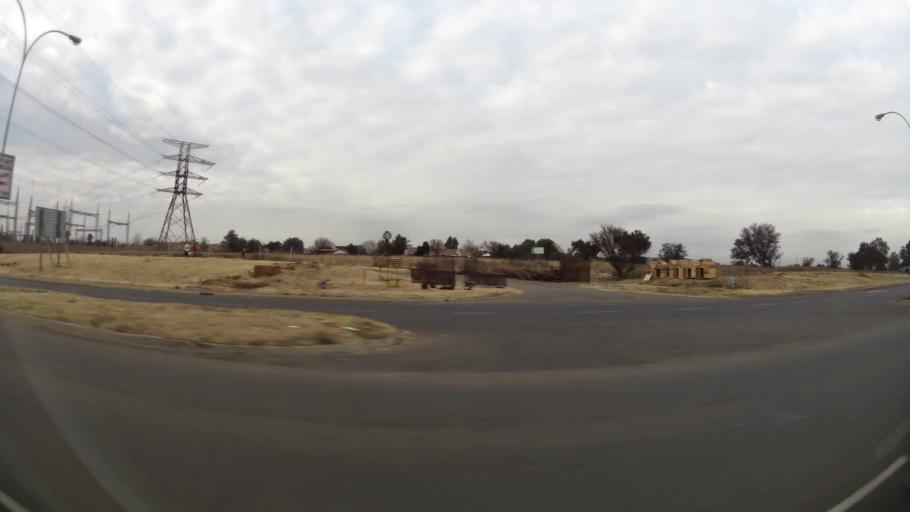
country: ZA
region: Orange Free State
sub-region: Mangaung Metropolitan Municipality
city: Bloemfontein
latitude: -29.1268
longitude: 26.1659
